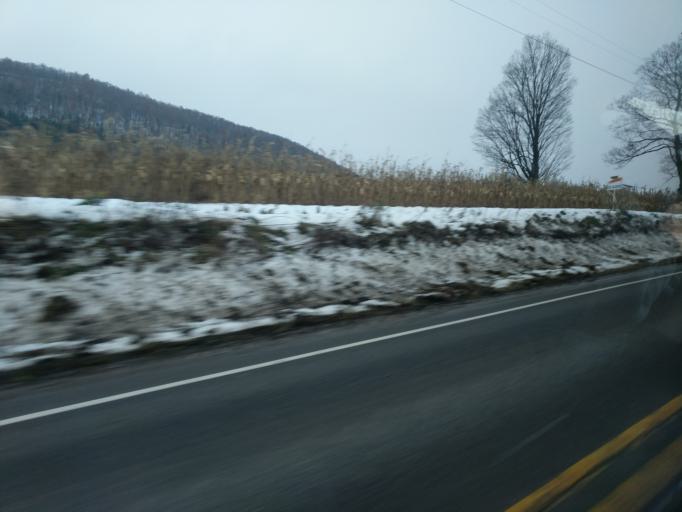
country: US
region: Pennsylvania
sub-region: Tioga County
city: Wellsboro
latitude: 41.8506
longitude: -77.2532
